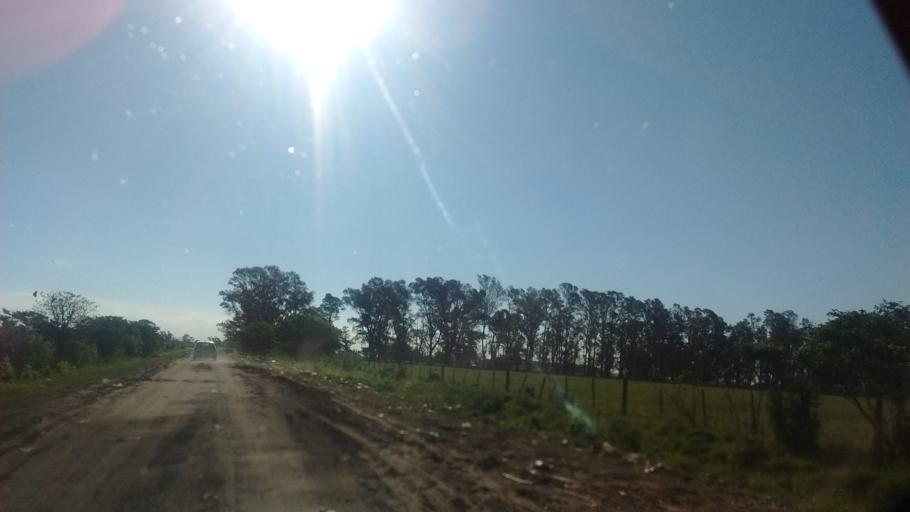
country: AR
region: Santa Fe
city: Funes
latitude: -32.8936
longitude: -60.8023
